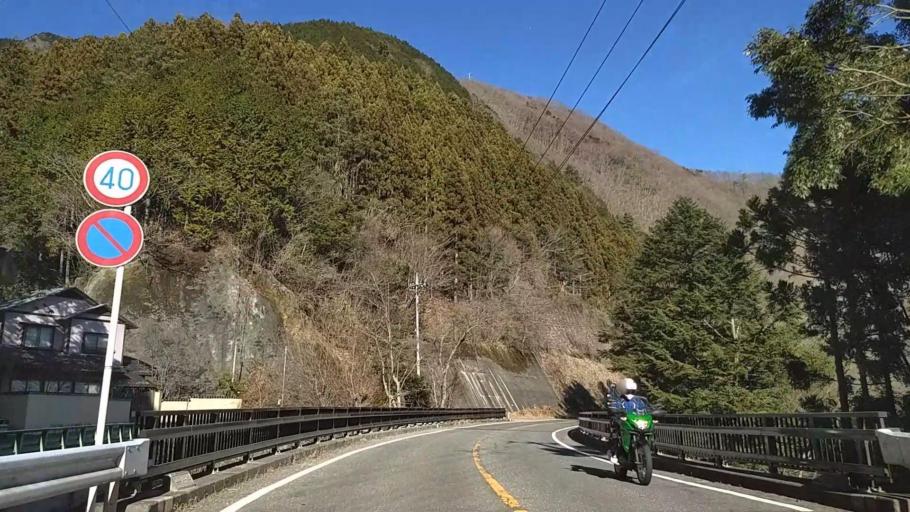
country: JP
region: Yamanashi
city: Uenohara
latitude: 35.5357
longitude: 139.0564
